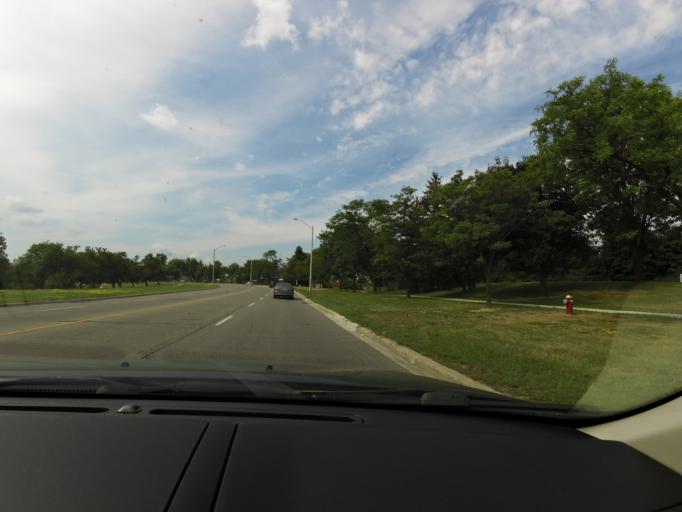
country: CA
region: Ontario
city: Brampton
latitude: 43.7277
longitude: -79.7269
